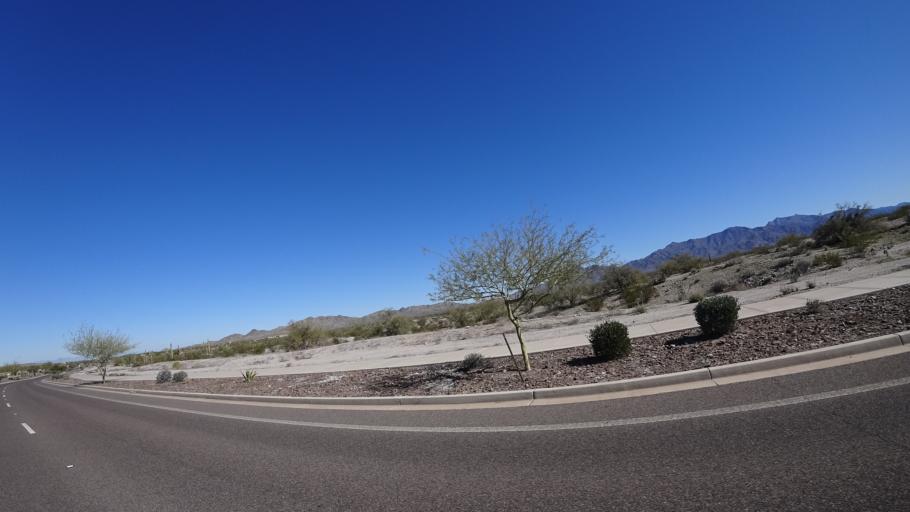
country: US
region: Arizona
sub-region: Maricopa County
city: Goodyear
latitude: 33.3107
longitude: -112.4337
